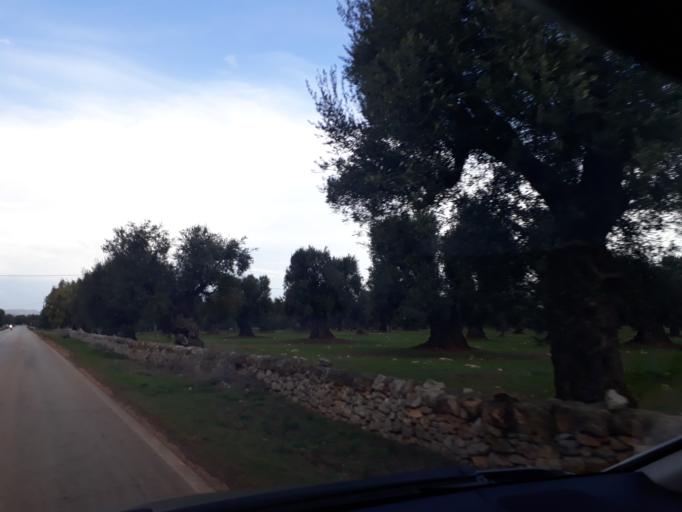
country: IT
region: Apulia
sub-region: Provincia di Brindisi
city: Pezze di Greco
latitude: 40.8094
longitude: 17.3870
